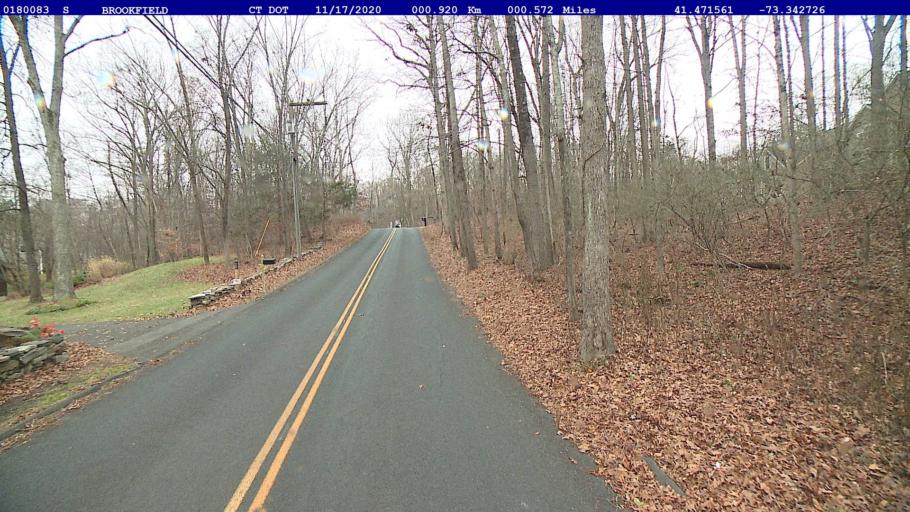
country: US
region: Connecticut
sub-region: Fairfield County
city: Newtown
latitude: 41.4716
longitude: -73.3427
